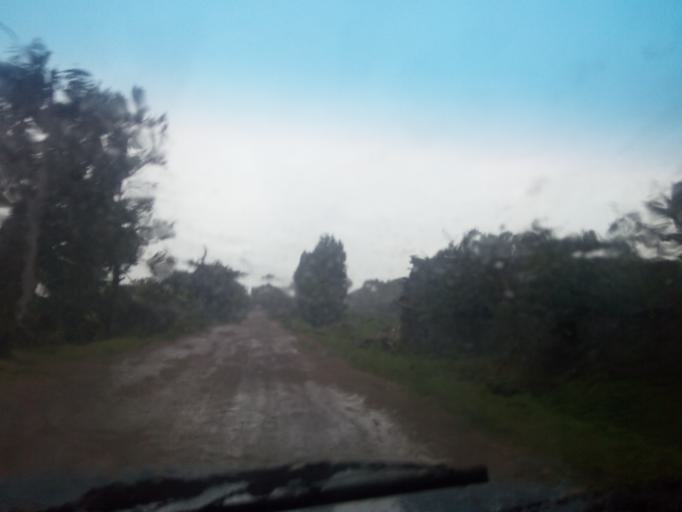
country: BY
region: Vitebsk
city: Dzisna
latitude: 55.6716
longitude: 28.3208
